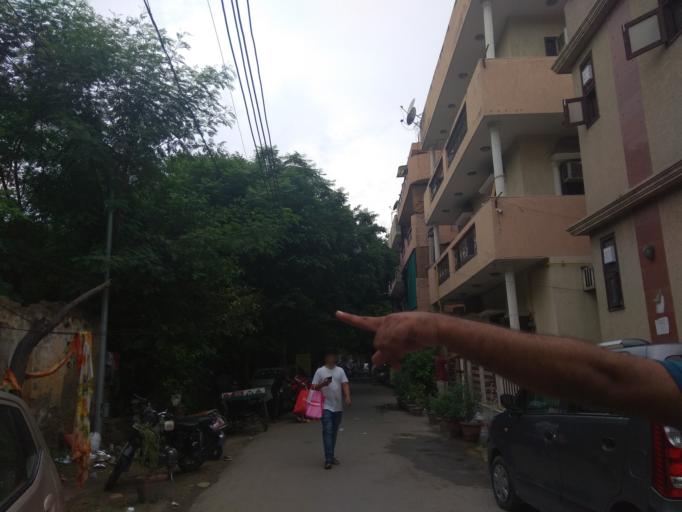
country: IN
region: NCT
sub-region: New Delhi
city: New Delhi
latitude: 28.5705
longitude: 77.2455
